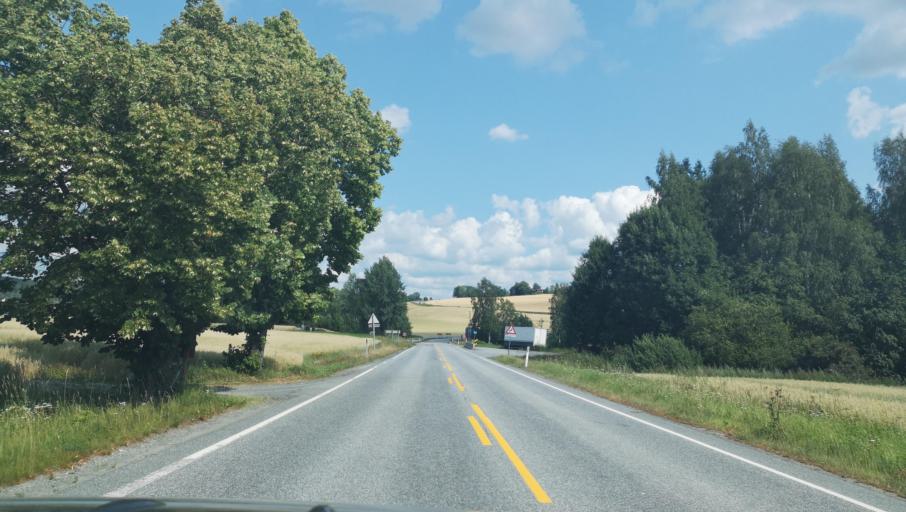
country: NO
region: Buskerud
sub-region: Ovre Eiker
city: Hokksund
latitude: 59.7243
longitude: 9.8322
